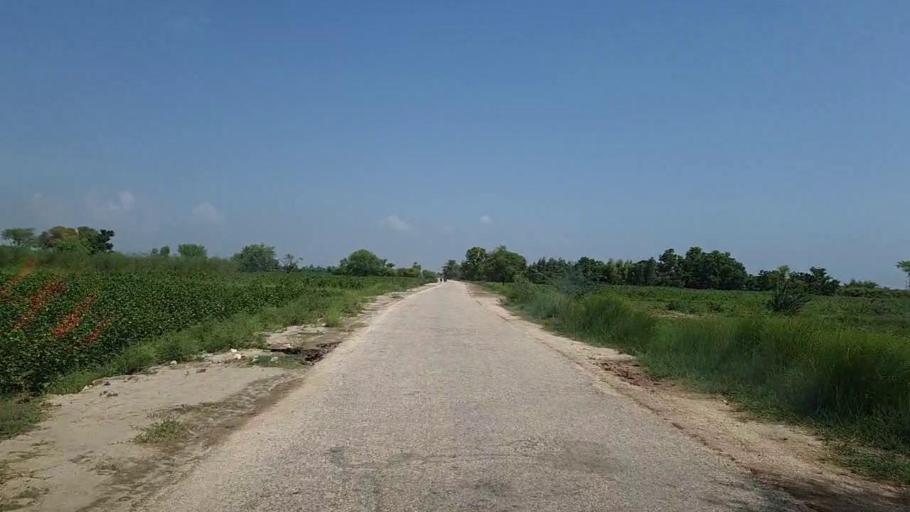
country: PK
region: Sindh
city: Bhiria
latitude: 26.8957
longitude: 68.2209
